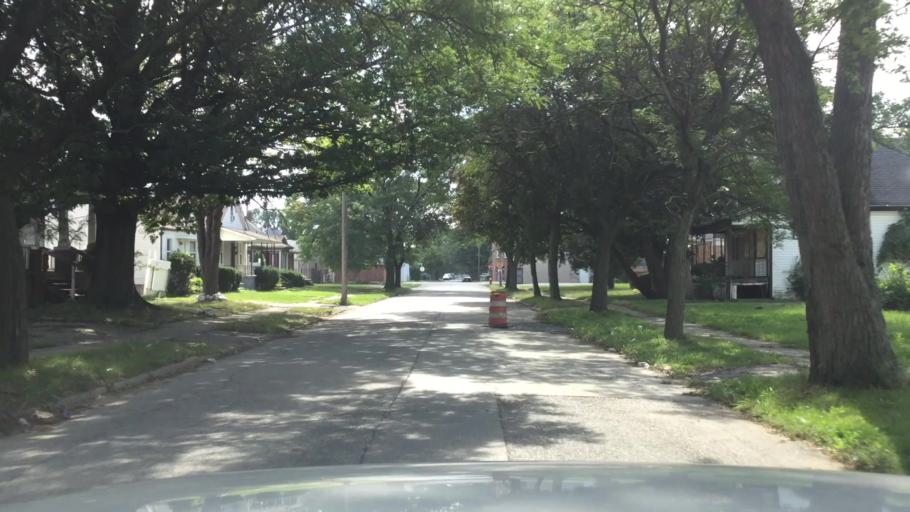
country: US
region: Michigan
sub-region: Wayne County
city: Dearborn Heights
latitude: 42.3446
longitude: -83.2232
